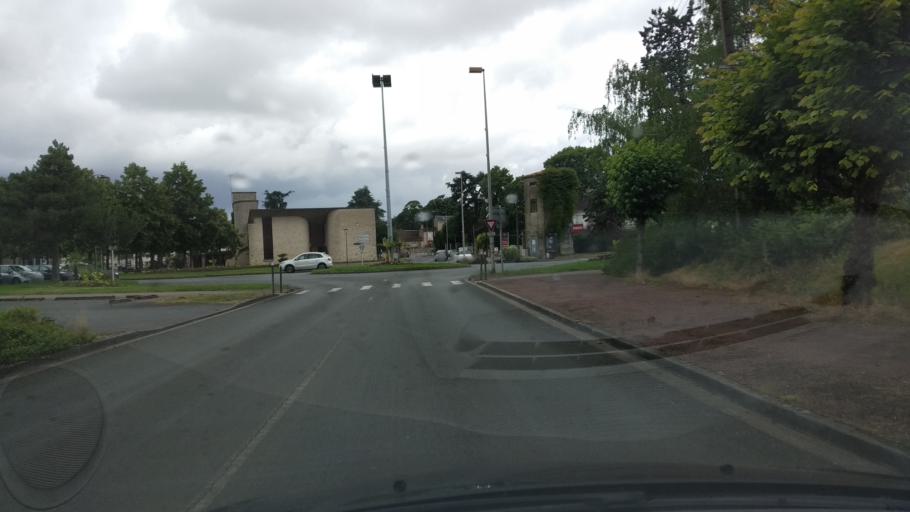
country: FR
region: Poitou-Charentes
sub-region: Departement de la Vienne
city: Saint-Benoit
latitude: 46.5666
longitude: 0.3444
